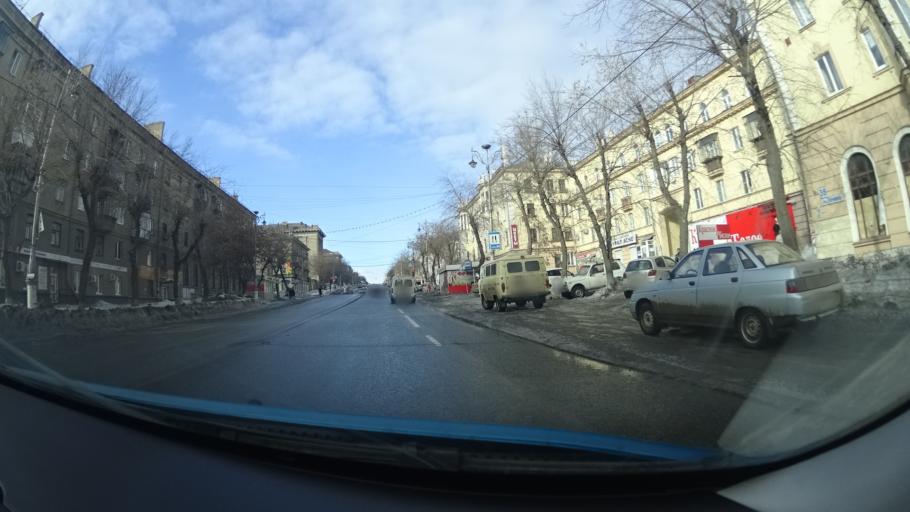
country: RU
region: Chelyabinsk
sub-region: Gorod Magnitogorsk
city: Magnitogorsk
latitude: 53.4251
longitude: 58.9837
